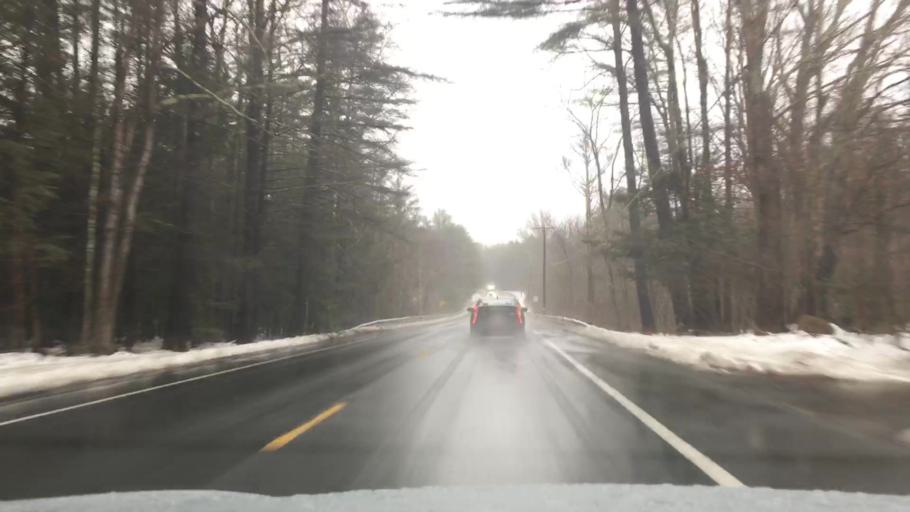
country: US
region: Massachusetts
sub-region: Franklin County
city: Shutesbury
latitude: 42.4828
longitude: -72.3436
